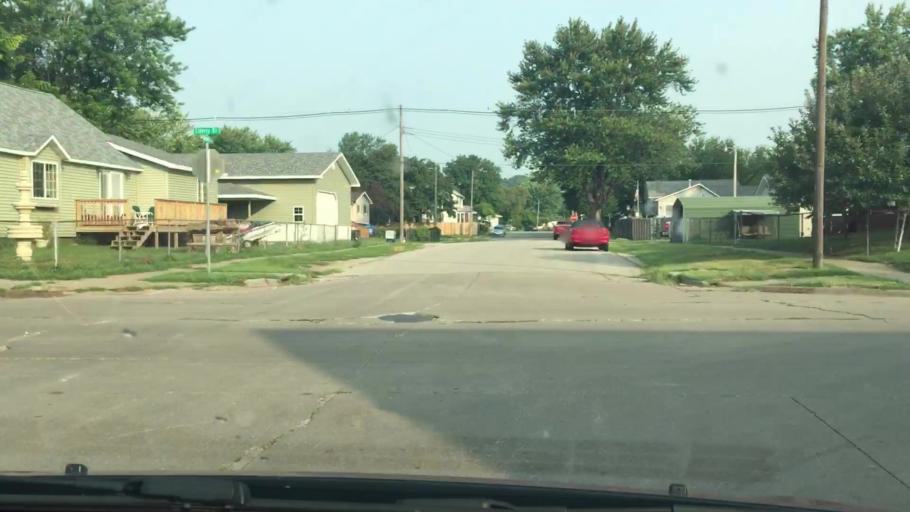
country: US
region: Iowa
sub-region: Muscatine County
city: Muscatine
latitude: 41.4101
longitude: -91.0637
